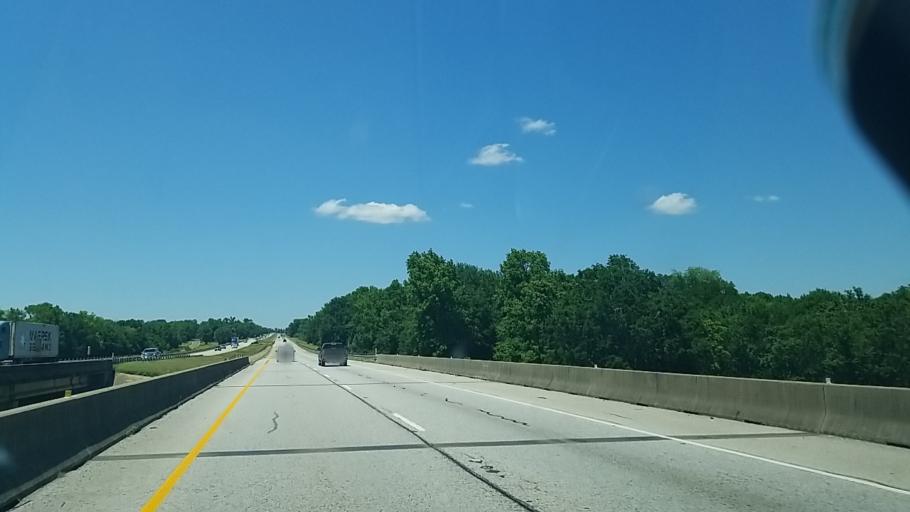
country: US
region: Texas
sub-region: Leon County
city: Centerville
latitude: 31.1849
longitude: -95.9910
